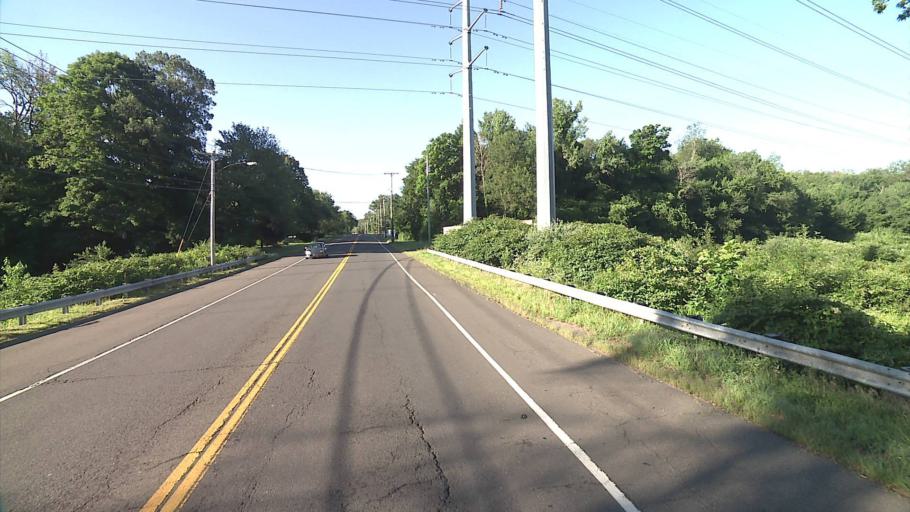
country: US
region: Connecticut
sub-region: New Haven County
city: Cheshire
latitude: 41.4487
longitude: -72.9100
